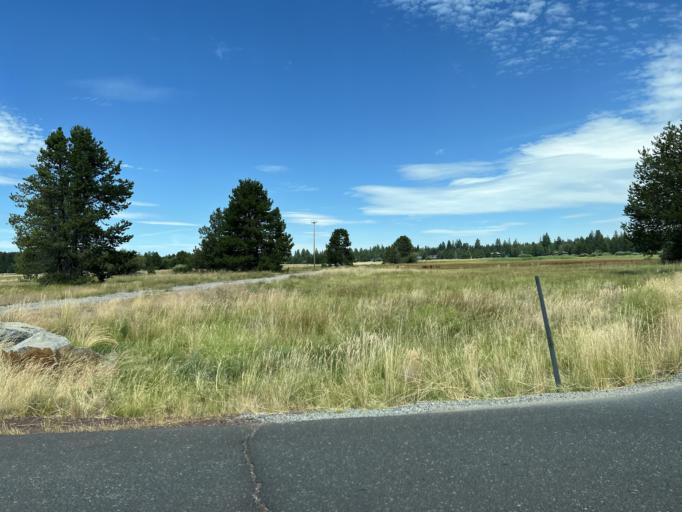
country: US
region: Oregon
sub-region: Deschutes County
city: Sunriver
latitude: 43.8846
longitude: -121.4530
